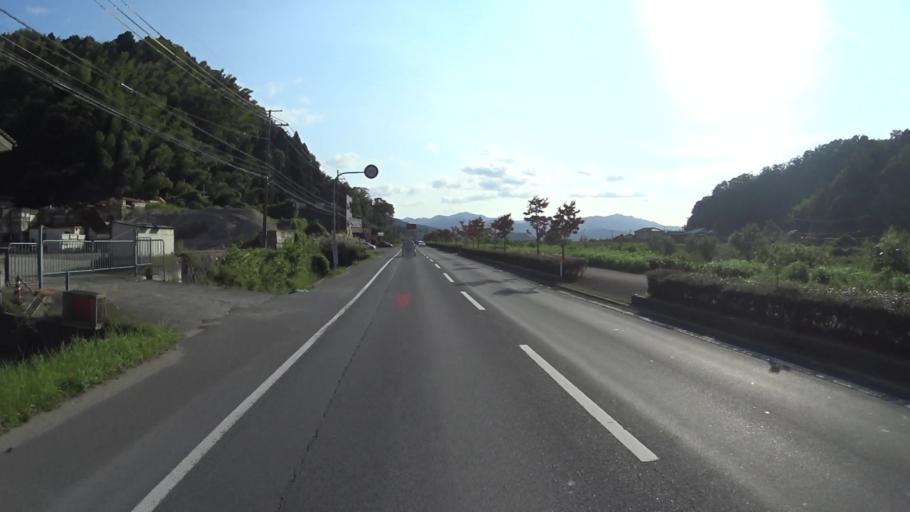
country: JP
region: Kyoto
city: Miyazu
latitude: 35.5487
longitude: 135.1370
